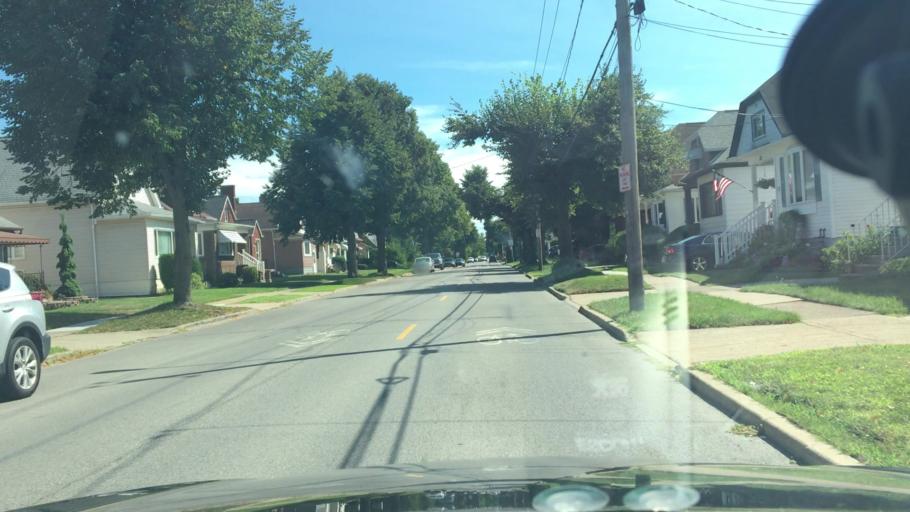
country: US
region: New York
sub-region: Erie County
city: West Seneca
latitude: 42.8704
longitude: -78.8021
